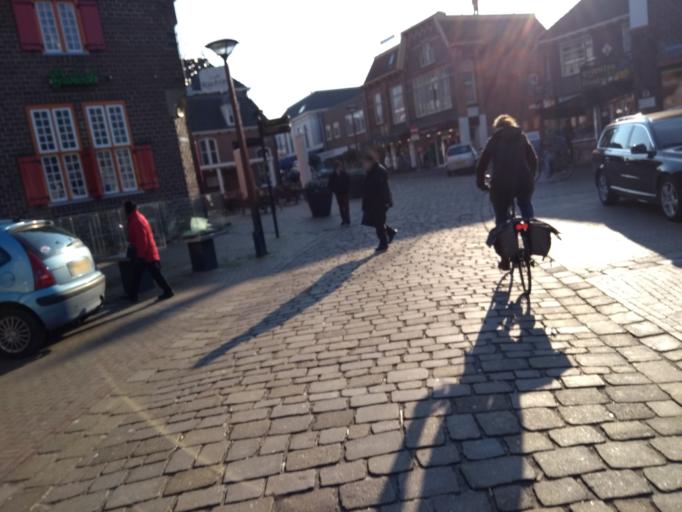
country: NL
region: Overijssel
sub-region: Gemeente Tubbergen
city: Tubbergen
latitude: 52.4080
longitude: 6.7819
